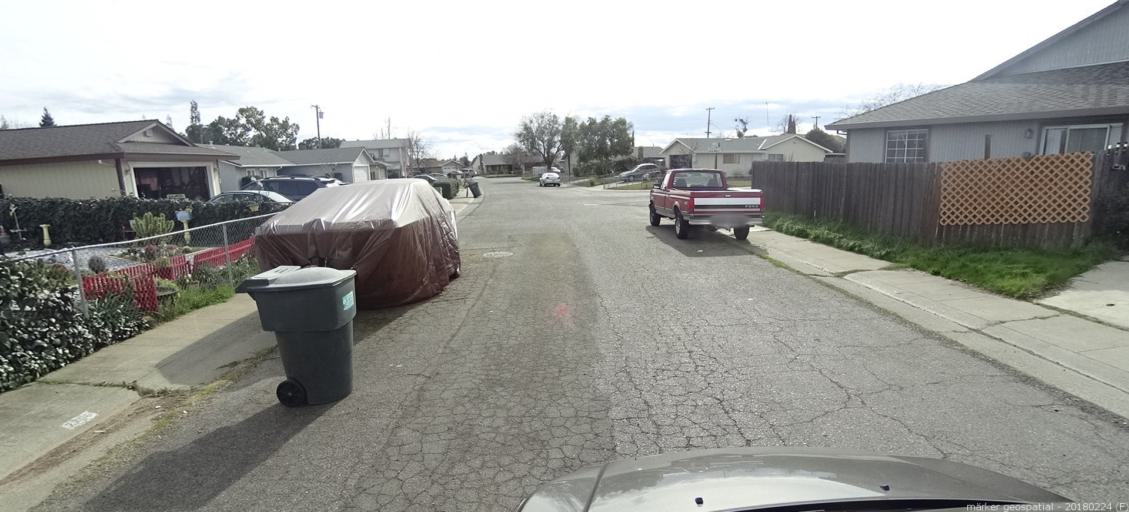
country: US
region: California
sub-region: Sacramento County
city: Rio Linda
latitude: 38.7065
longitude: -121.4390
